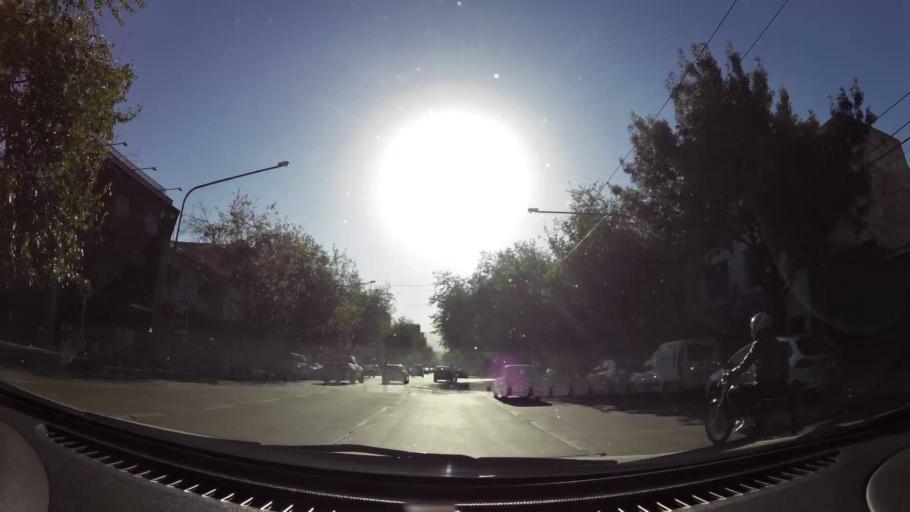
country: AR
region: Mendoza
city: Mendoza
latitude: -32.8958
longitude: -68.8359
